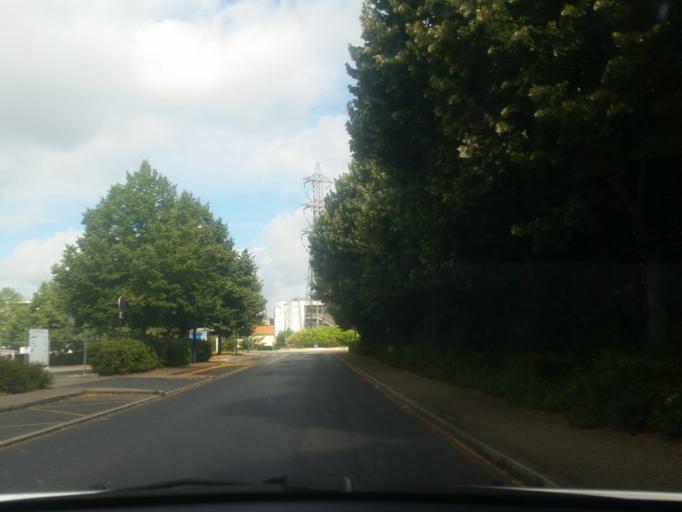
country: FR
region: Pays de la Loire
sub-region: Departement de la Loire-Atlantique
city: Sainte-Luce-sur-Loire
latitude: 47.2483
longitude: -1.5165
